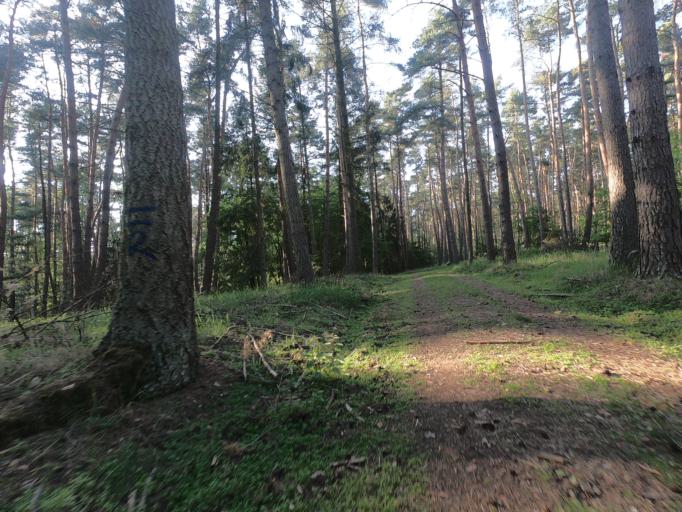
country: DE
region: Hesse
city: Morfelden-Walldorf
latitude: 50.0161
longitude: 8.5431
